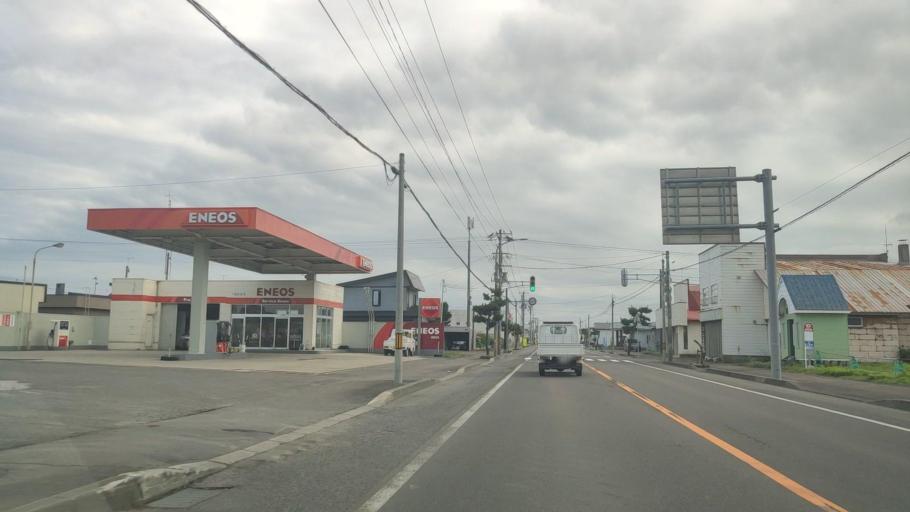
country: JP
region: Hokkaido
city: Niseko Town
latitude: 42.4384
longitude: 140.3235
